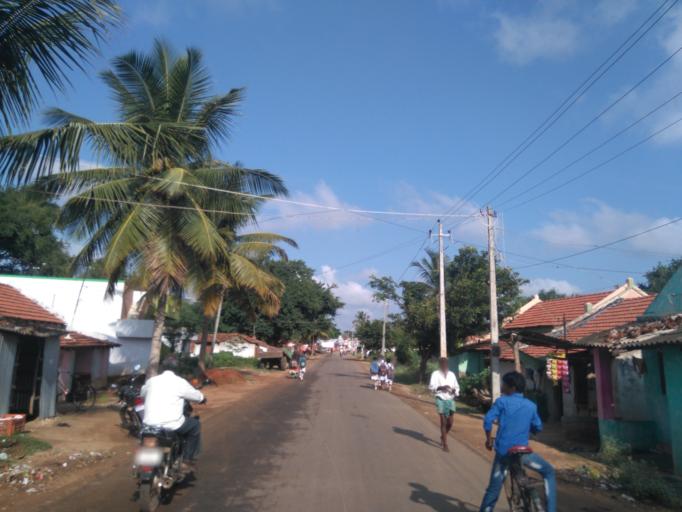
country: IN
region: Karnataka
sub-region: Mysore
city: Tirumakudal Narsipur
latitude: 12.2582
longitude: 76.9758
